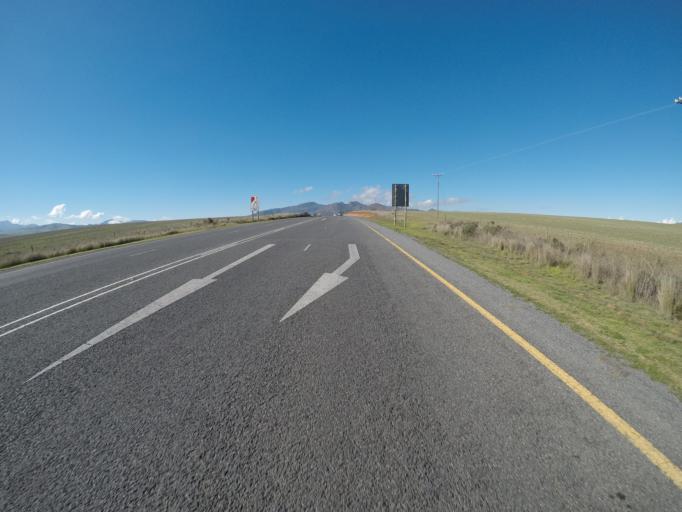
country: ZA
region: Western Cape
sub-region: Overberg District Municipality
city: Caledon
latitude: -34.2104
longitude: 19.3788
